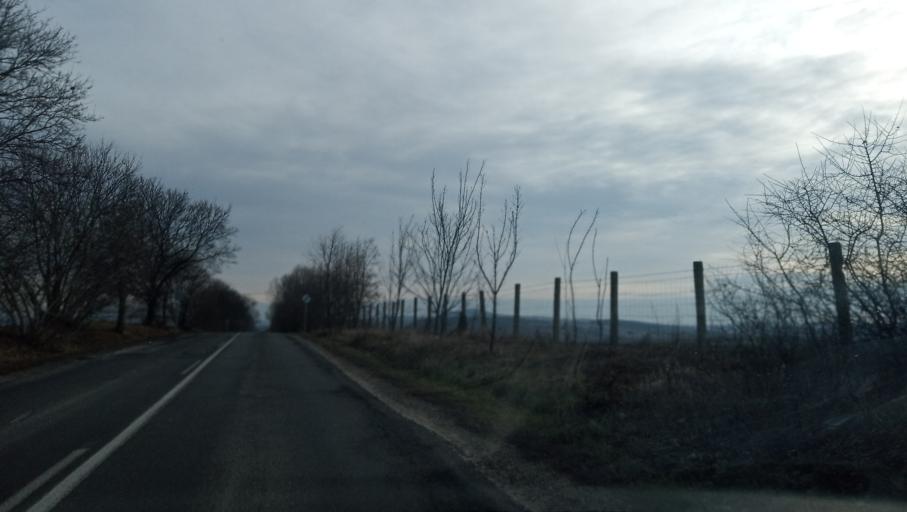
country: HU
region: Pest
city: Kosd
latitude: 47.7686
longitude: 19.1911
